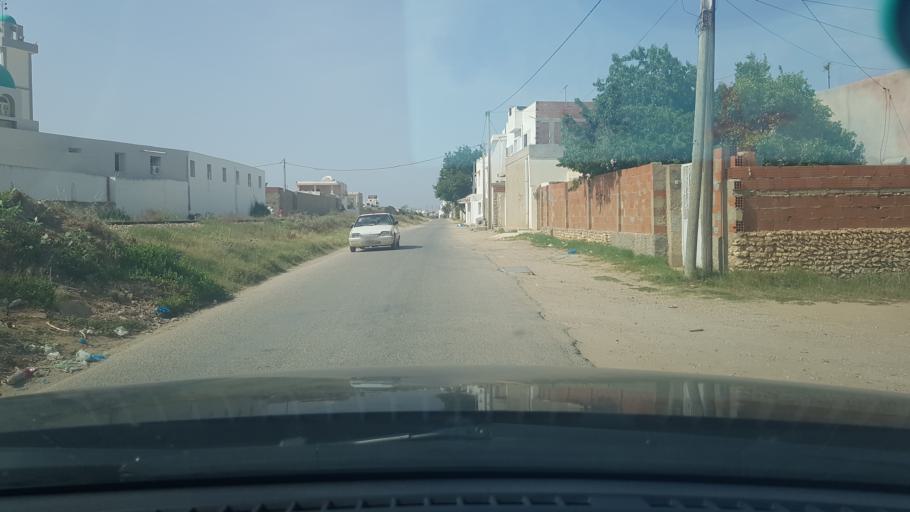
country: TN
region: Safaqis
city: Al Qarmadah
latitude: 34.8209
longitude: 10.7632
